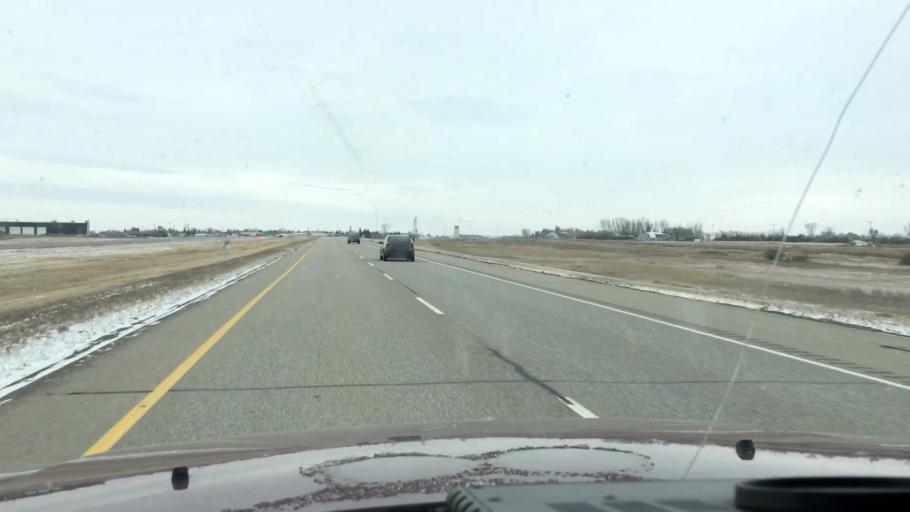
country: CA
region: Saskatchewan
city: Watrous
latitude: 51.2779
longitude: -106.0122
